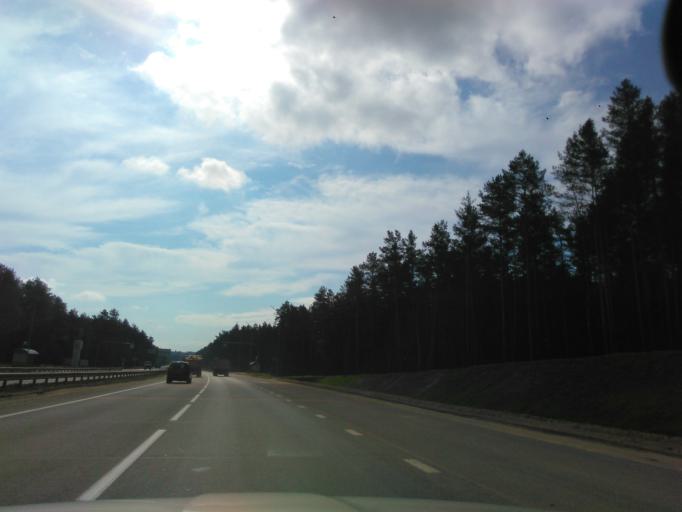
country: BY
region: Minsk
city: Rakaw
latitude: 53.9632
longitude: 27.0930
